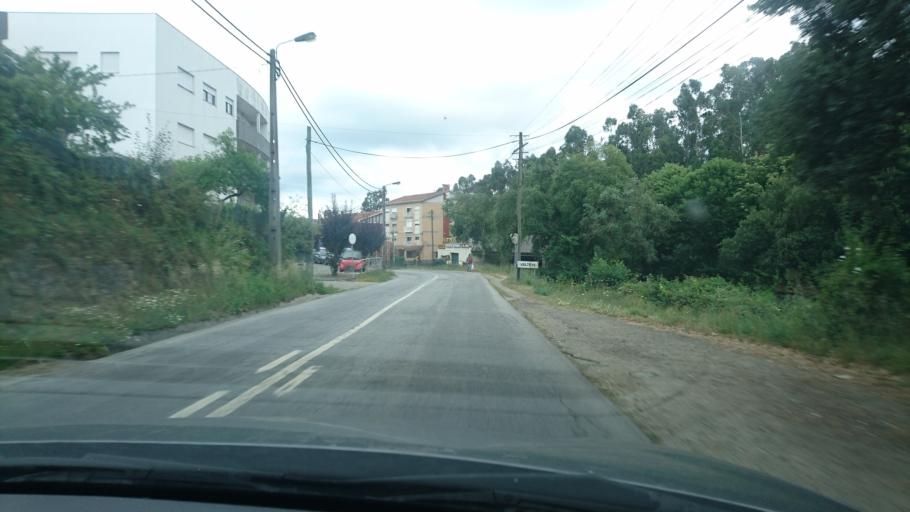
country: PT
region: Porto
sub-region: Paredes
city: Recarei
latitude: 41.1570
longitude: -8.4201
